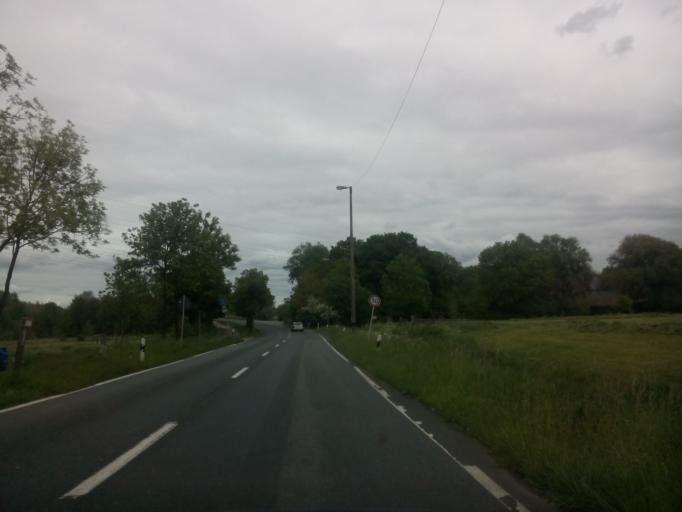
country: DE
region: Lower Saxony
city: Stuhr
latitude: 53.0780
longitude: 8.7302
